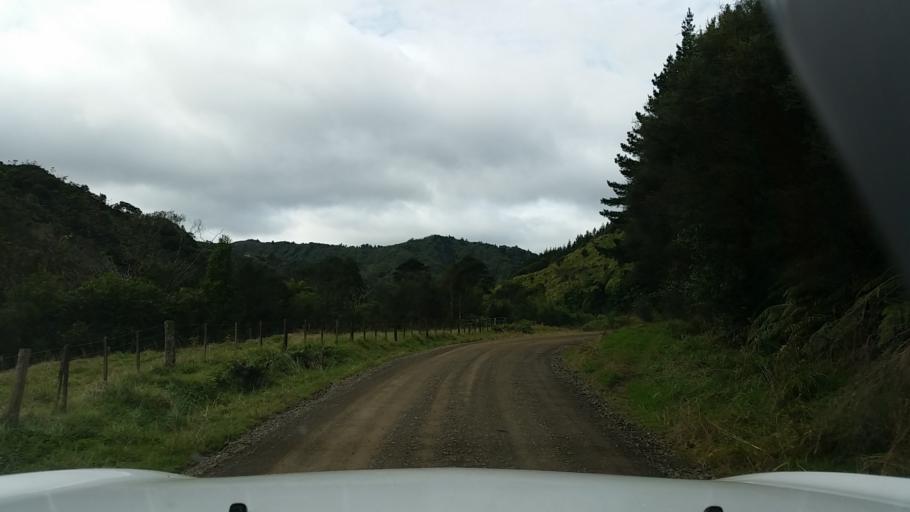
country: NZ
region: Taranaki
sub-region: New Plymouth District
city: Waitara
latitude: -38.8971
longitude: 174.7536
